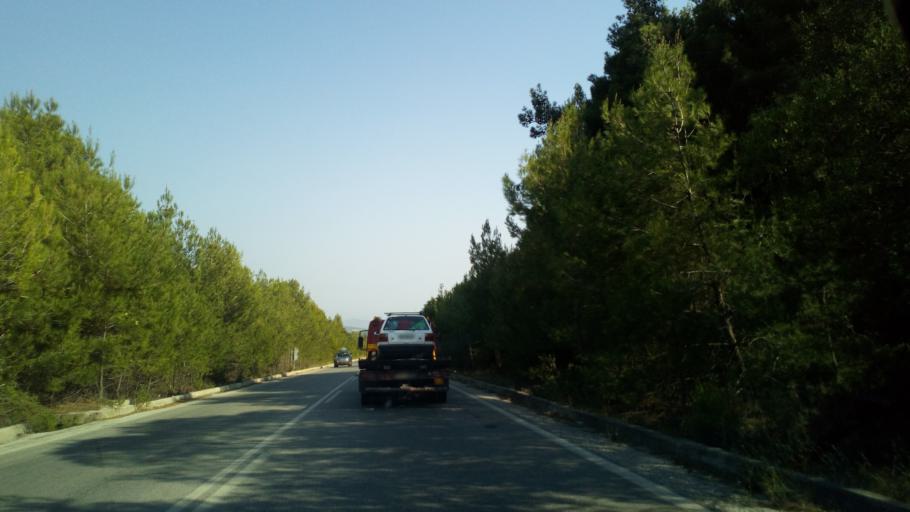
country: GR
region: Central Macedonia
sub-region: Nomos Chalkidikis
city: Polygyros
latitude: 40.3575
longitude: 23.4395
